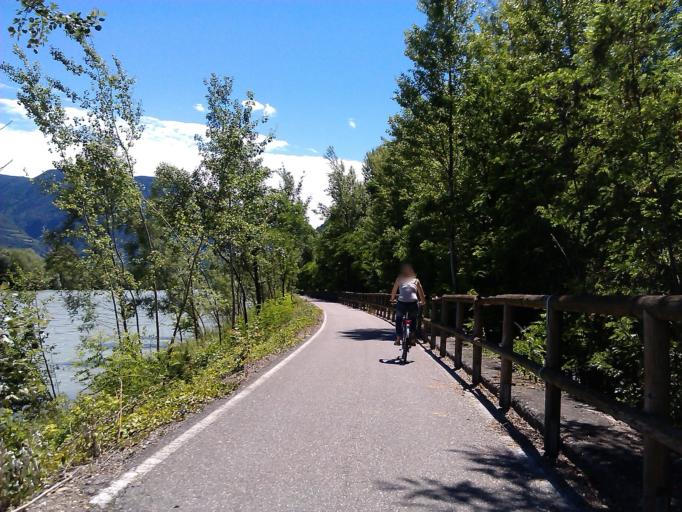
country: IT
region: Trentino-Alto Adige
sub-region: Bolzano
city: Cornaiano
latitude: 46.4567
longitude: 11.3021
